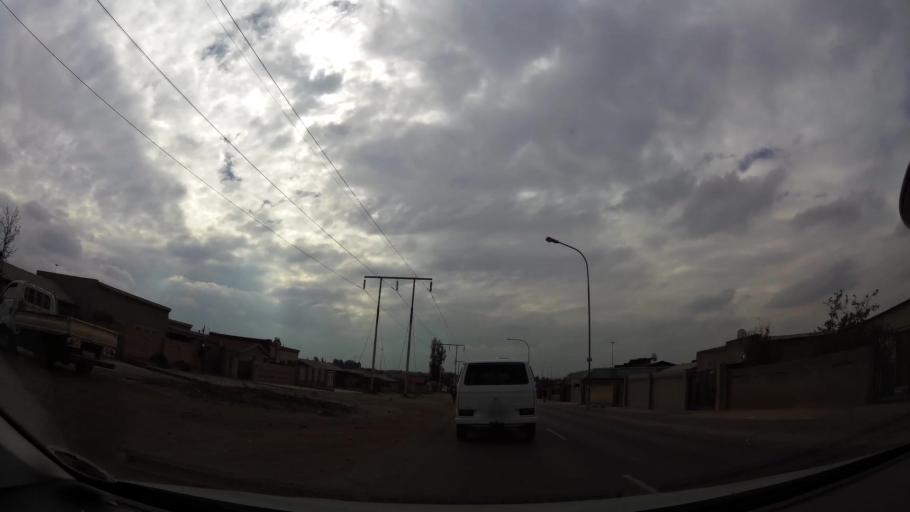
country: ZA
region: Gauteng
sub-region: City of Johannesburg Metropolitan Municipality
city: Soweto
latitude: -26.2724
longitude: 27.8606
